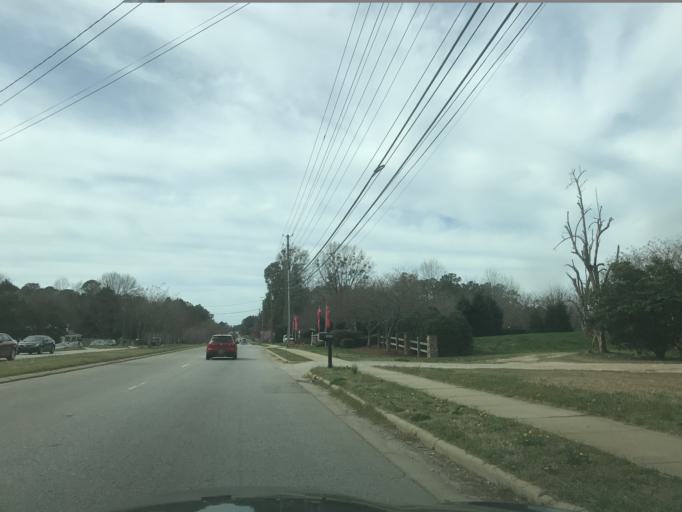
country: US
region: North Carolina
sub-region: Wake County
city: West Raleigh
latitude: 35.7432
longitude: -78.6868
